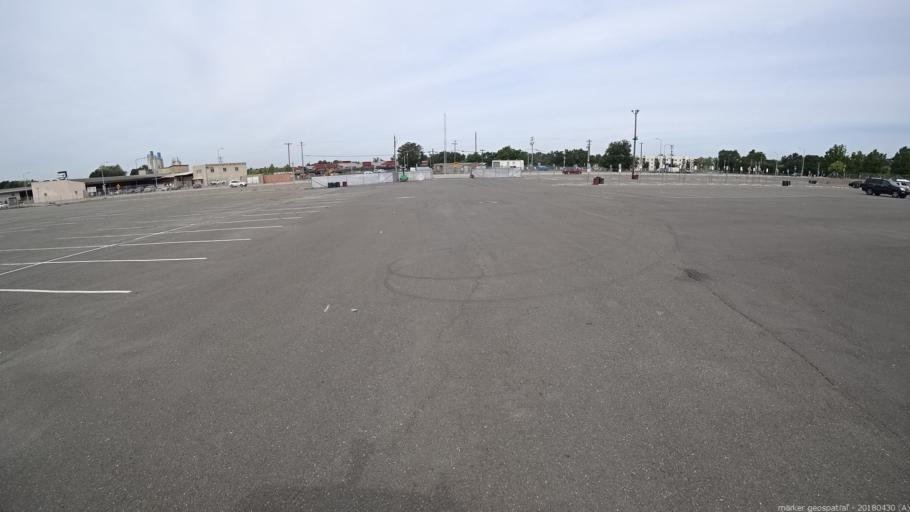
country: US
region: California
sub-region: Yolo County
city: West Sacramento
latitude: 38.5782
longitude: -121.5149
